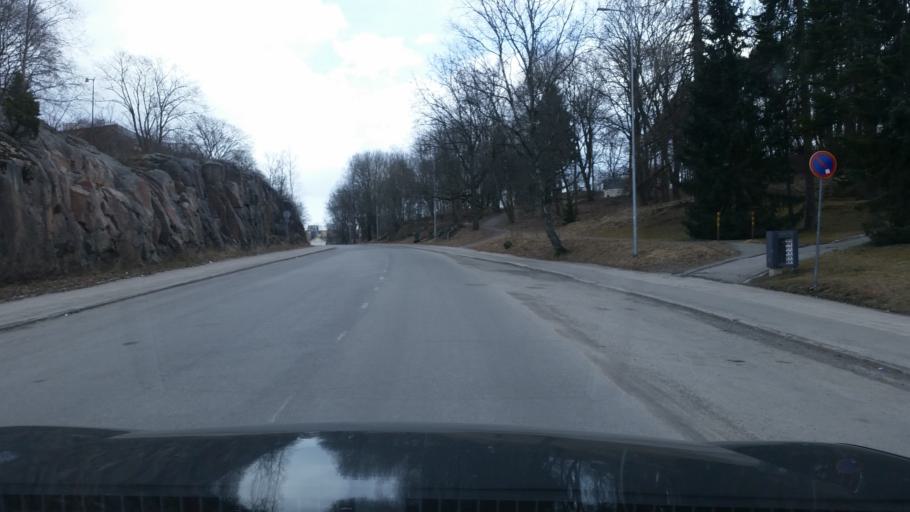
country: FI
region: Varsinais-Suomi
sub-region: Turku
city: Turku
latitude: 60.4449
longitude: 22.2650
